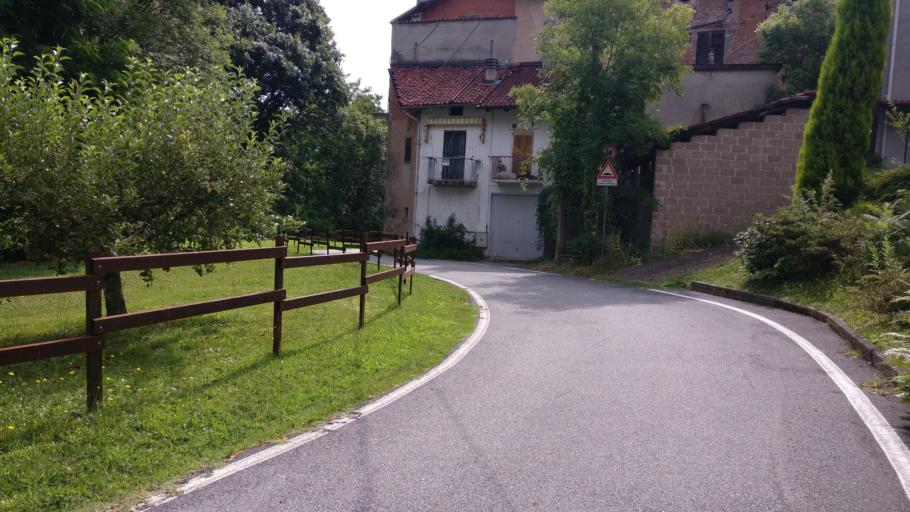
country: IT
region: Piedmont
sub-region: Provincia di Vercelli
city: Roasio
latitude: 45.6023
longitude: 8.2829
